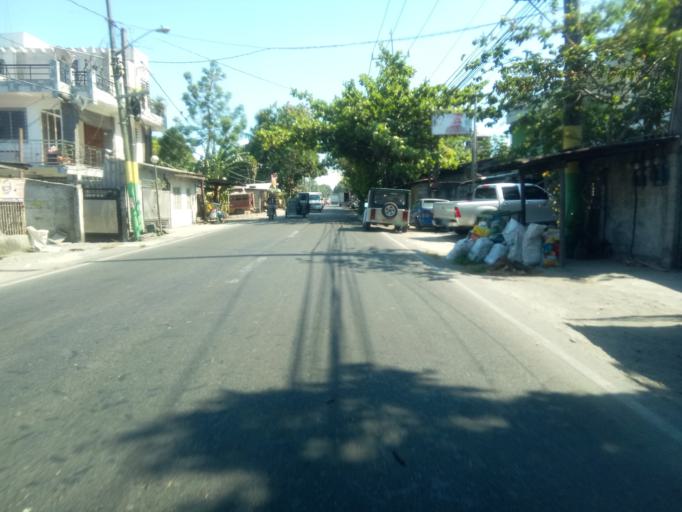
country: PH
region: Calabarzon
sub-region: Province of Cavite
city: Bulihan
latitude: 14.2978
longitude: 120.9912
